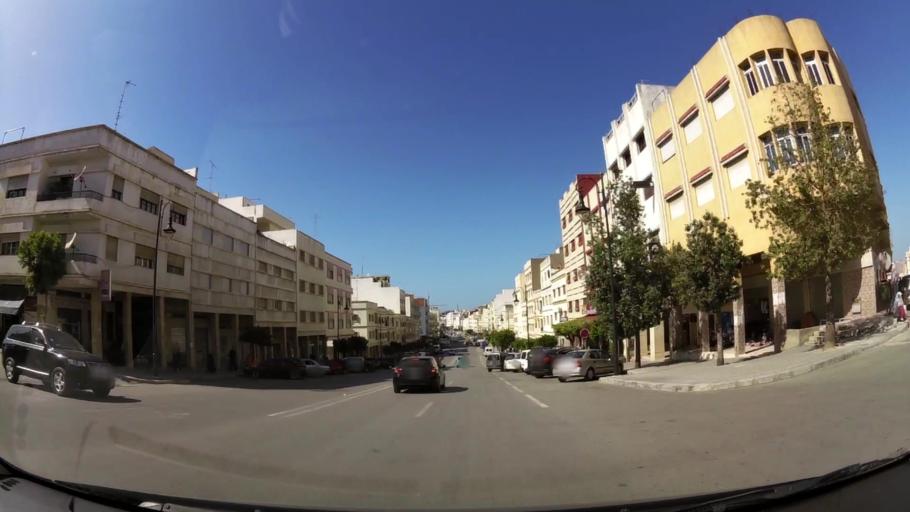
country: MA
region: Tanger-Tetouan
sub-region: Tanger-Assilah
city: Tangier
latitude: 35.7496
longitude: -5.8091
